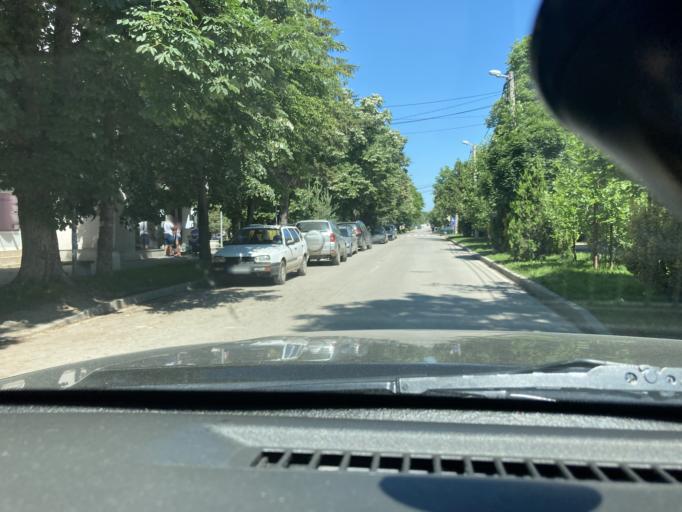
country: BG
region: Sofiya
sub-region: Obshtina Slivnitsa
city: Slivnitsa
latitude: 42.8531
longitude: 23.0373
